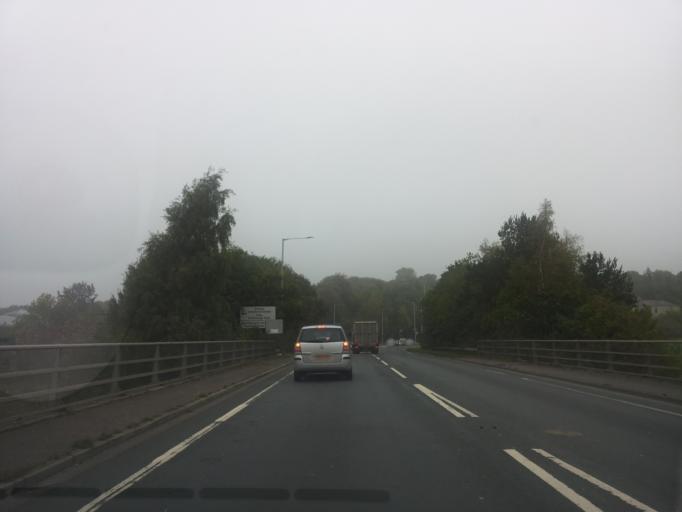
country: GB
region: England
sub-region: Lancashire
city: Padiham
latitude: 53.7957
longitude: -2.3346
